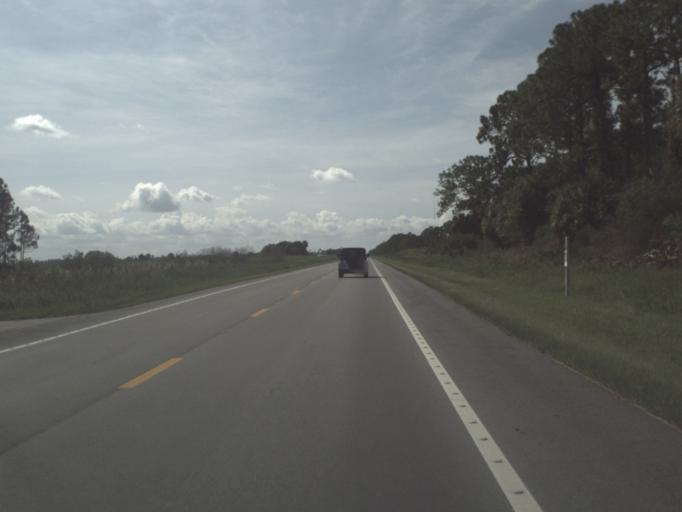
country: US
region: Florida
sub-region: Lee County
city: Olga
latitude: 26.8927
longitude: -81.7601
